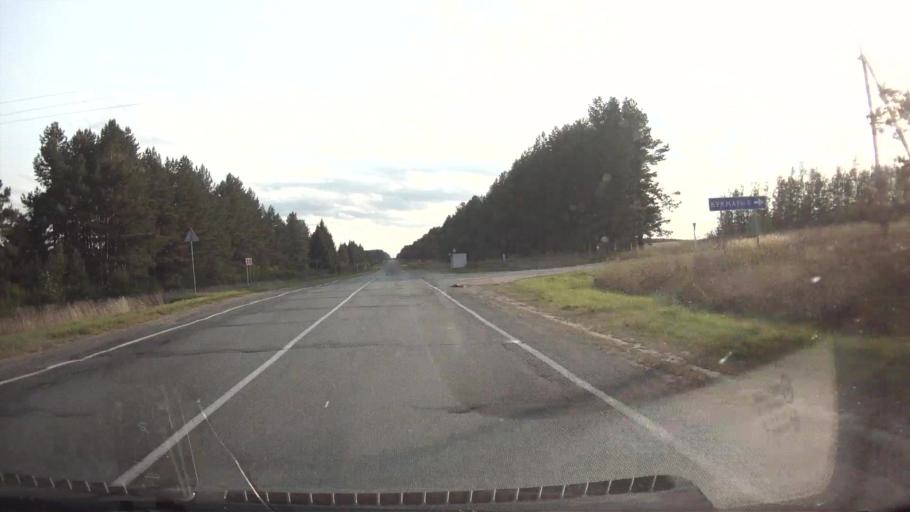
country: RU
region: Mariy-El
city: Kuzhener
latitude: 56.8484
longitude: 48.7455
